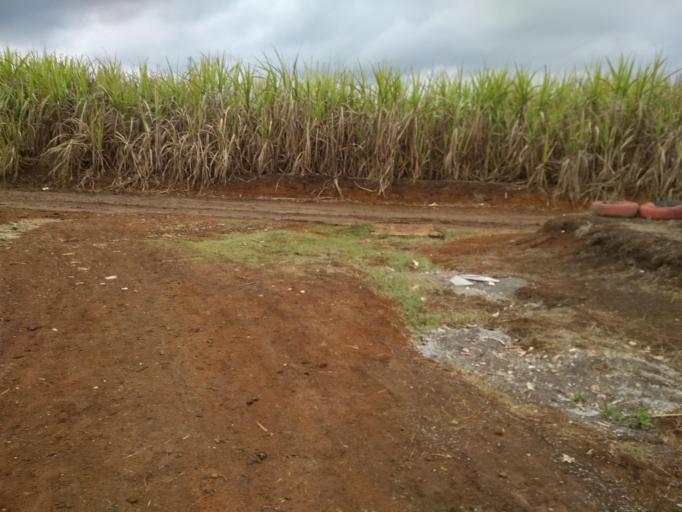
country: MX
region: Veracruz
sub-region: Cordoba
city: San Jose de Tapia
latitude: 18.8507
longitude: -96.9625
